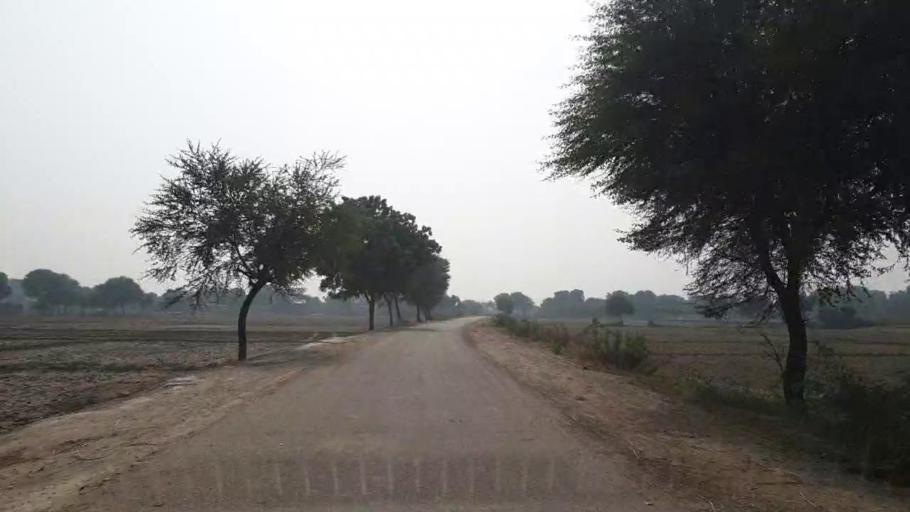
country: PK
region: Sindh
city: Tando Muhammad Khan
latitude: 25.1856
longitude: 68.6242
